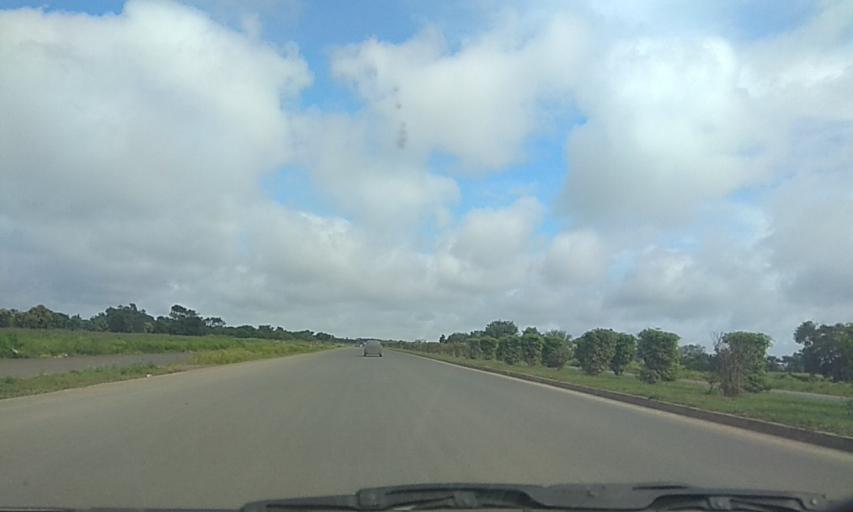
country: IN
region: Karnataka
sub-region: Haveri
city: Shiggaon
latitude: 14.9983
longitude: 75.2092
